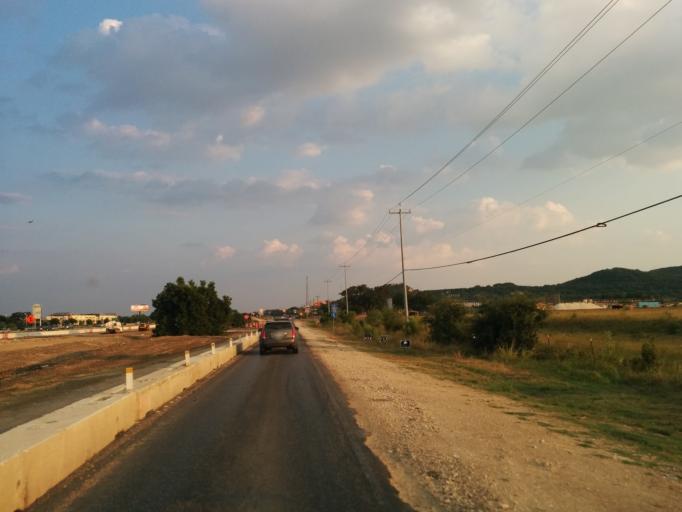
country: US
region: Texas
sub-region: Bexar County
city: Cross Mountain
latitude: 29.6722
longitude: -98.6347
